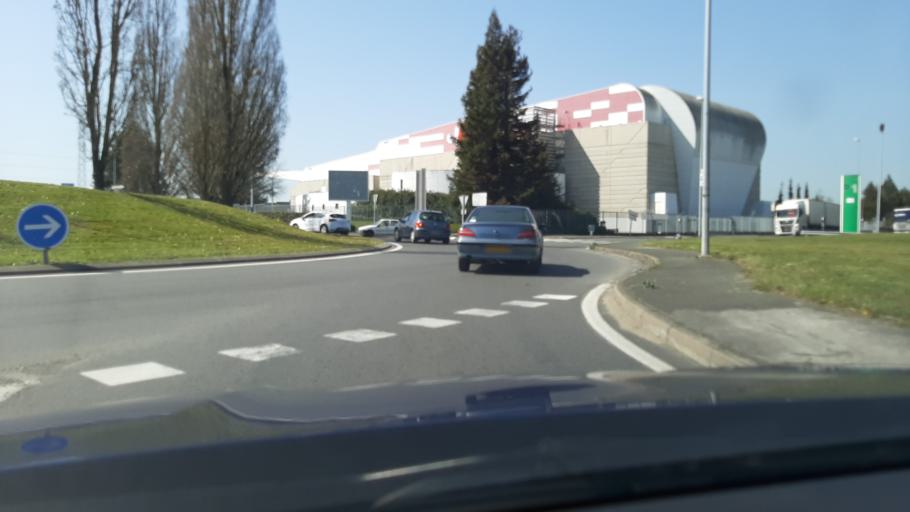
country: FR
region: Pays de la Loire
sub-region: Departement de Maine-et-Loire
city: Ecouflant
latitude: 47.4978
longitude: -0.4922
